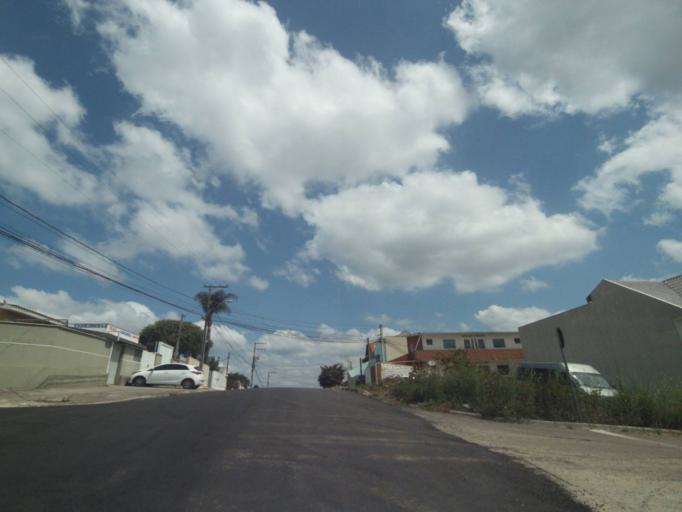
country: BR
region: Parana
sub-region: Curitiba
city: Curitiba
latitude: -25.5033
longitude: -49.3064
